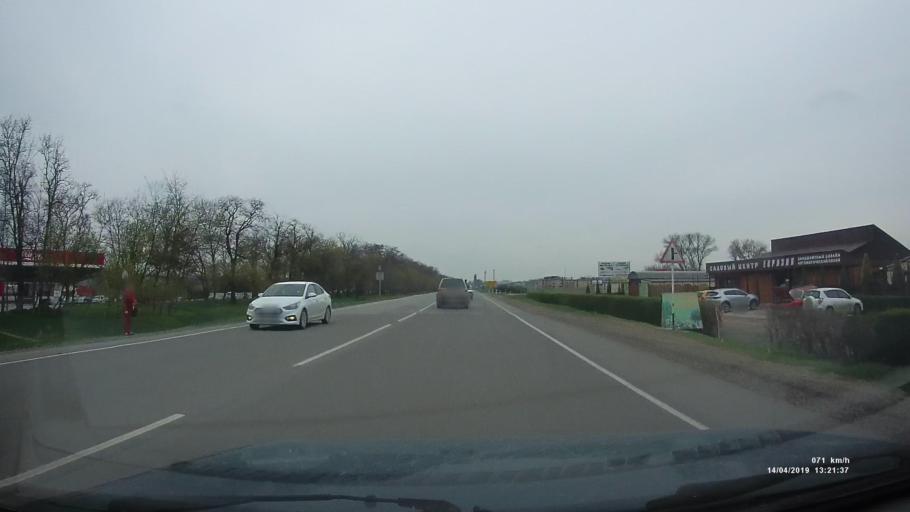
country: RU
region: Rostov
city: Kuleshovka
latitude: 47.0817
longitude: 39.5223
